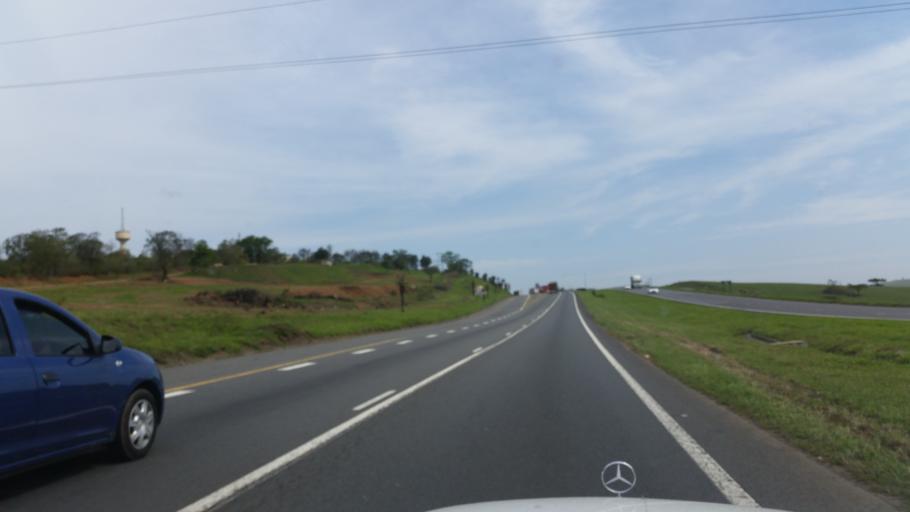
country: ZA
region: KwaZulu-Natal
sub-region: uMgungundlovu District Municipality
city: Camperdown
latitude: -29.7106
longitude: 30.4963
